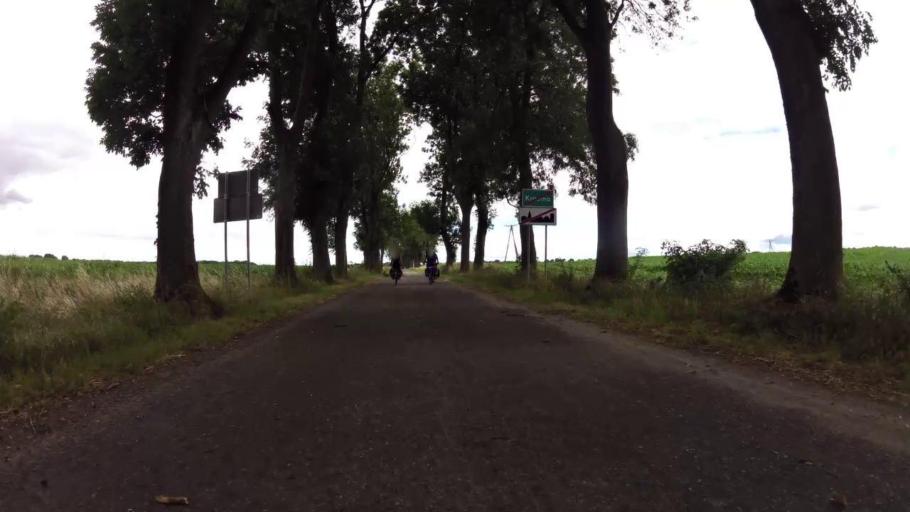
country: PL
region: West Pomeranian Voivodeship
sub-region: Powiat lobeski
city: Lobez
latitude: 53.7585
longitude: 15.5768
